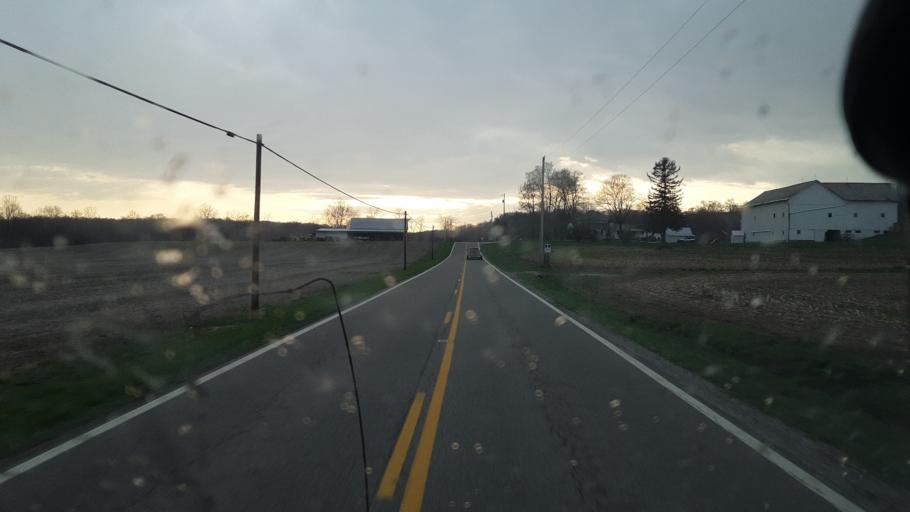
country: US
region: Ohio
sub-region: Licking County
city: Utica
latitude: 40.1635
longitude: -82.4750
